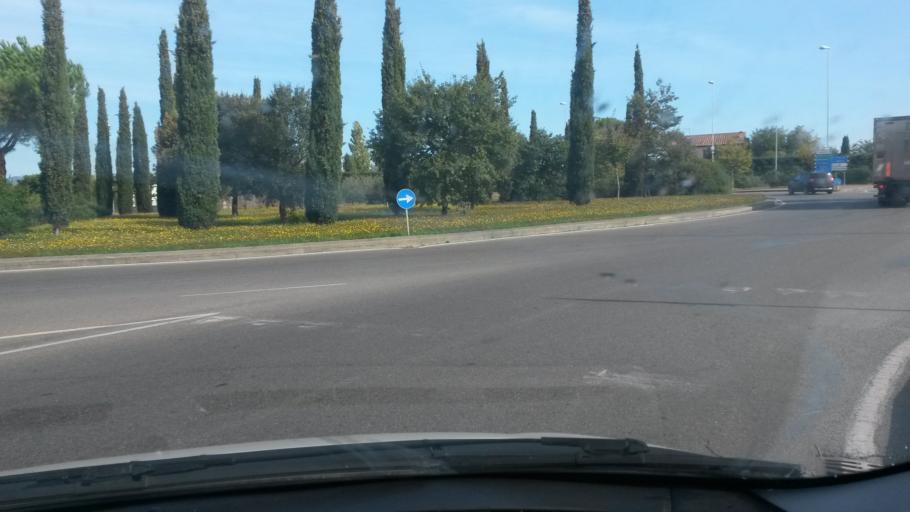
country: IT
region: Tuscany
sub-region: Provincia di Livorno
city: Cecina
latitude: 43.3139
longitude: 10.5333
